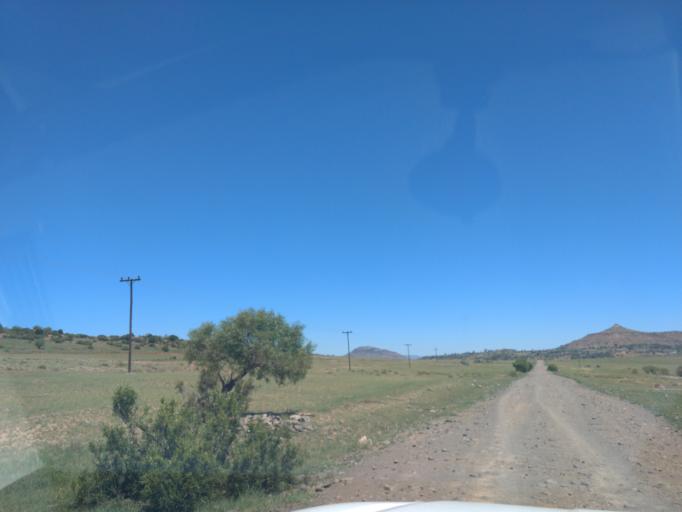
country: LS
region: Maseru
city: Maseru
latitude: -29.4707
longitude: 27.3755
